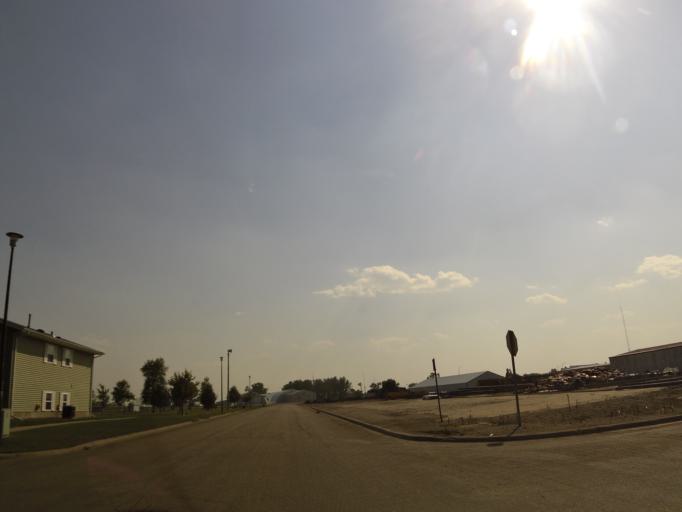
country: US
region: North Dakota
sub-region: Walsh County
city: Grafton
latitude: 48.4146
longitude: -97.4055
